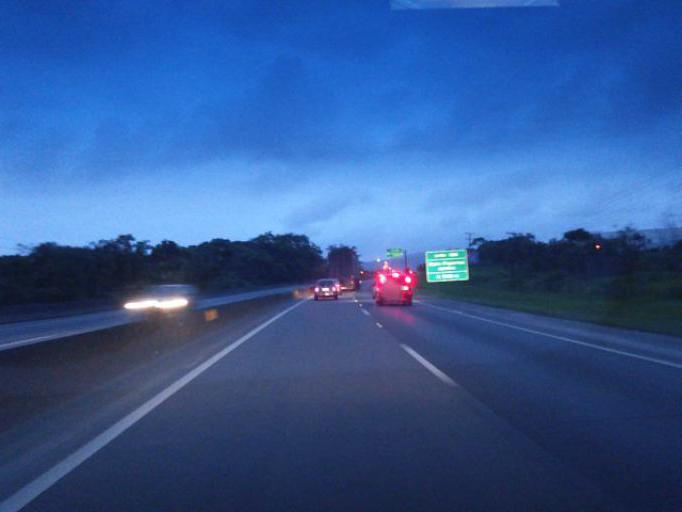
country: BR
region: Santa Catarina
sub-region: Penha
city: Penha
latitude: -26.7529
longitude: -48.6910
